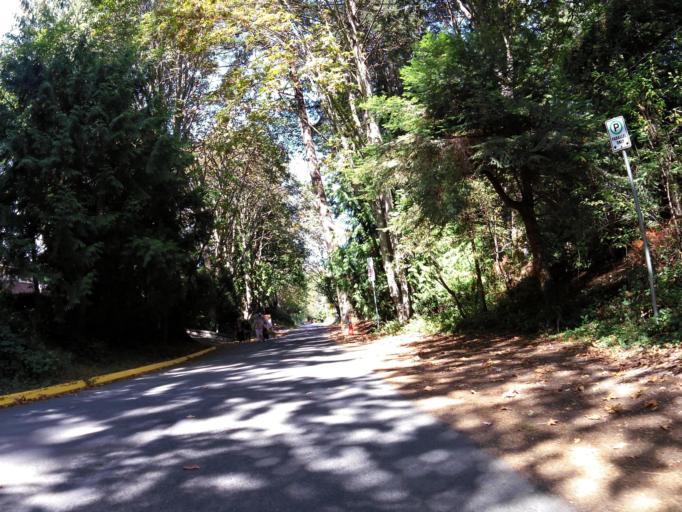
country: CA
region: British Columbia
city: Victoria
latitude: 48.5331
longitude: -123.3762
